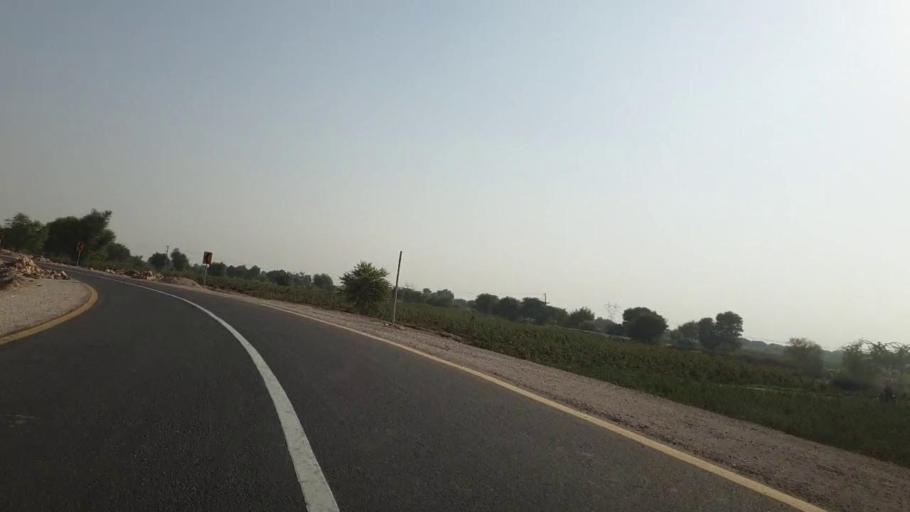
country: PK
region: Sindh
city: Bhan
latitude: 26.4835
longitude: 67.7794
